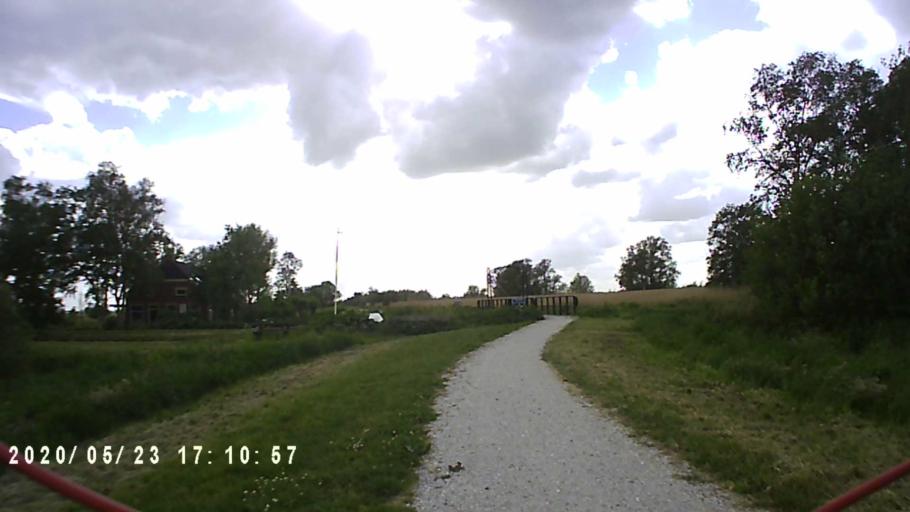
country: NL
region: Groningen
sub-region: Gemeente Slochteren
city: Slochteren
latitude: 53.2673
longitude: 6.8146
